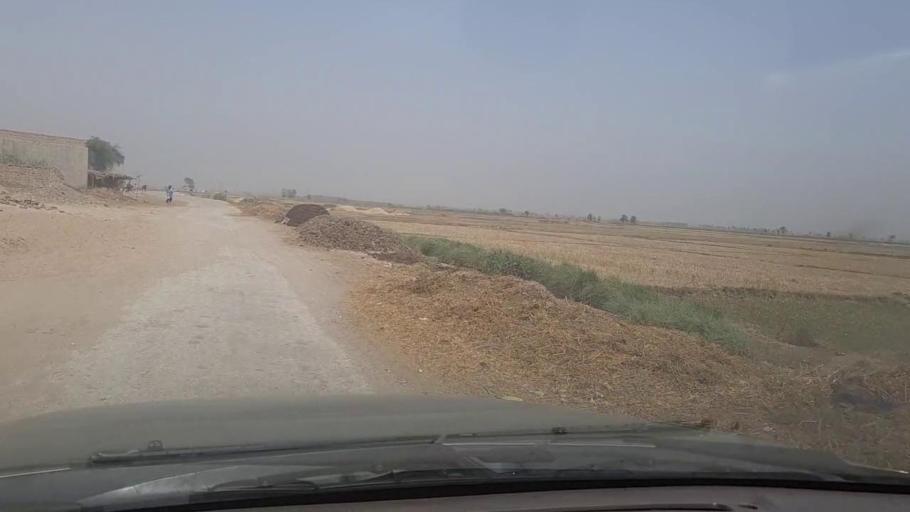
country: PK
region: Sindh
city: Madeji
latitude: 27.8028
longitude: 68.4032
